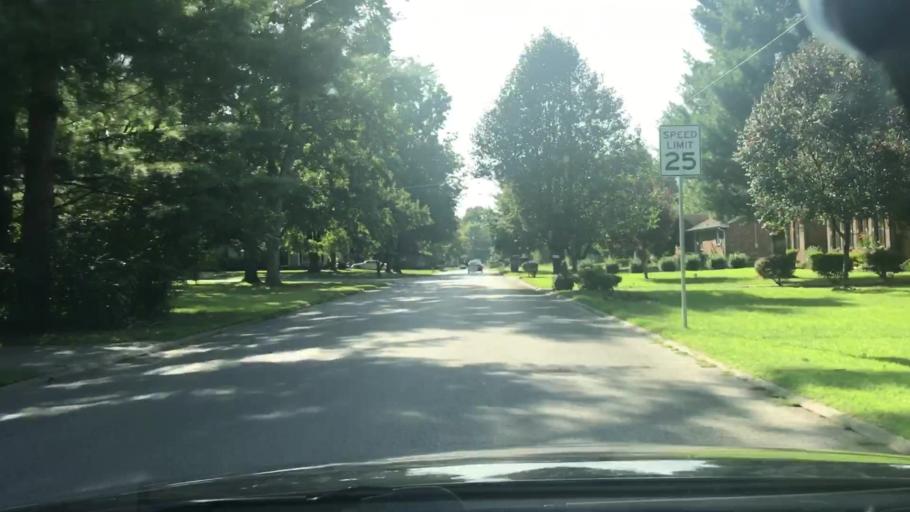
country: US
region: Tennessee
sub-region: Williamson County
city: Franklin
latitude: 35.9307
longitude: -86.8831
